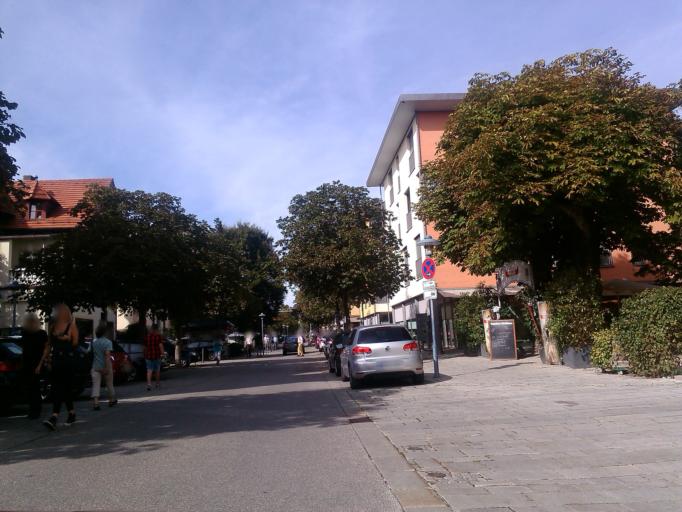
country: DE
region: Bavaria
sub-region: Upper Bavaria
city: Starnberg
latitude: 47.9968
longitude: 11.3434
